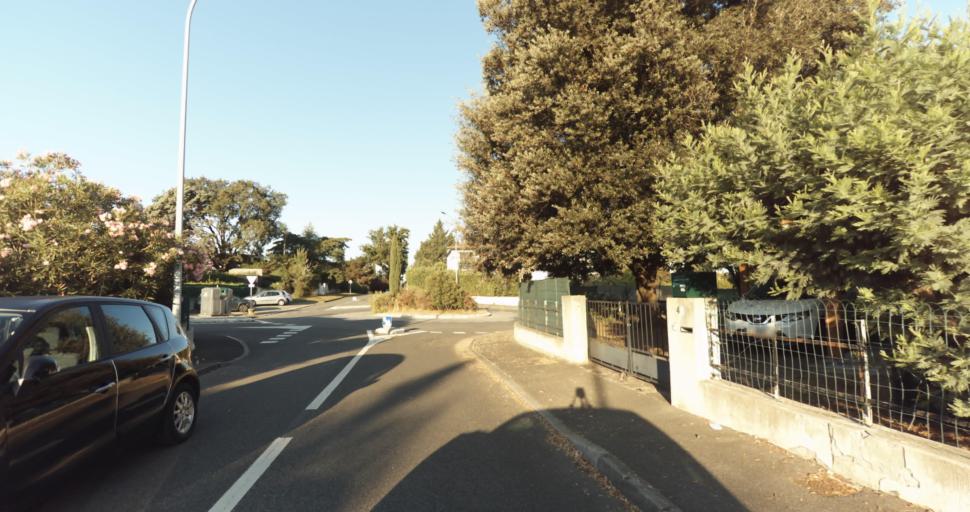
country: FR
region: Midi-Pyrenees
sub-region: Departement de la Haute-Garonne
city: L'Union
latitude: 43.6621
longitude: 1.4796
